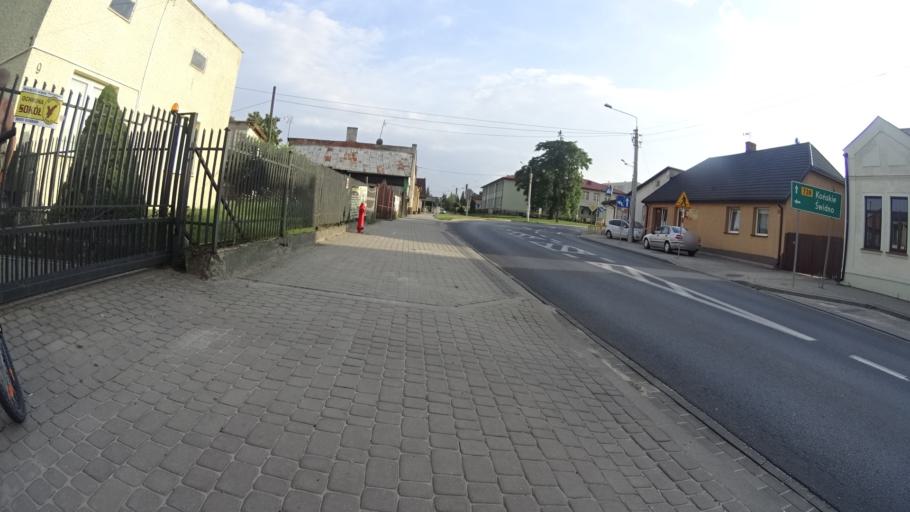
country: PL
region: Masovian Voivodeship
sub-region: Powiat grojecki
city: Mogielnica
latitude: 51.6917
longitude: 20.7215
